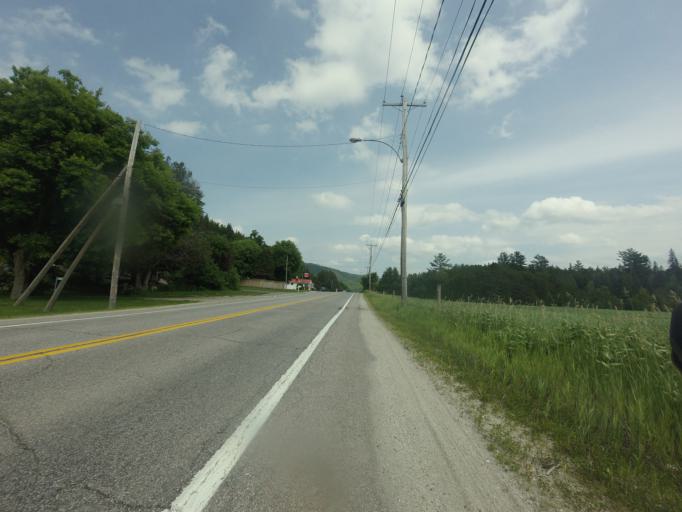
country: CA
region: Quebec
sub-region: Outaouais
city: Wakefield
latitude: 45.7614
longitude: -75.9295
